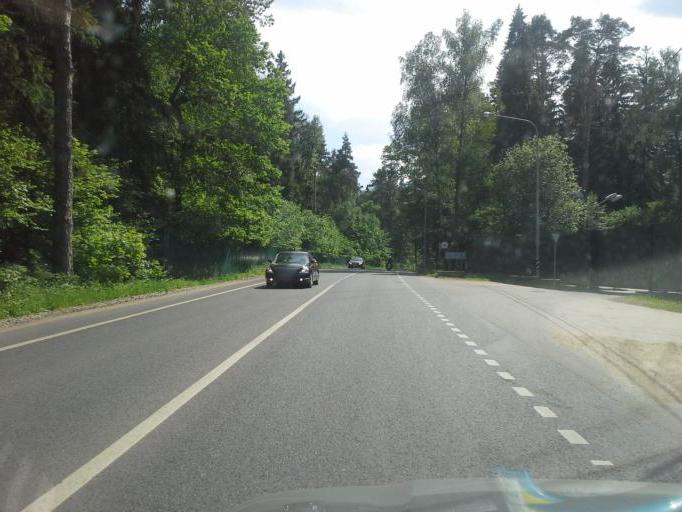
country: RU
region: Moskovskaya
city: Gorki Vtoryye
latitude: 55.7105
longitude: 37.1649
